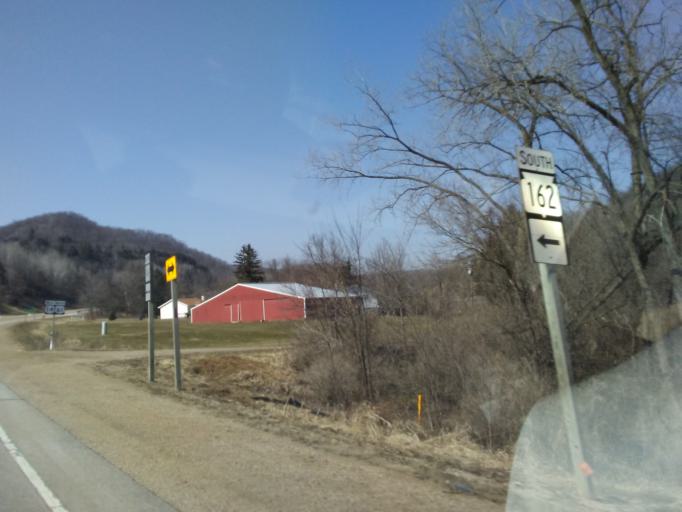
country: US
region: Wisconsin
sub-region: Vernon County
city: Westby
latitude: 43.7013
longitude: -91.0399
